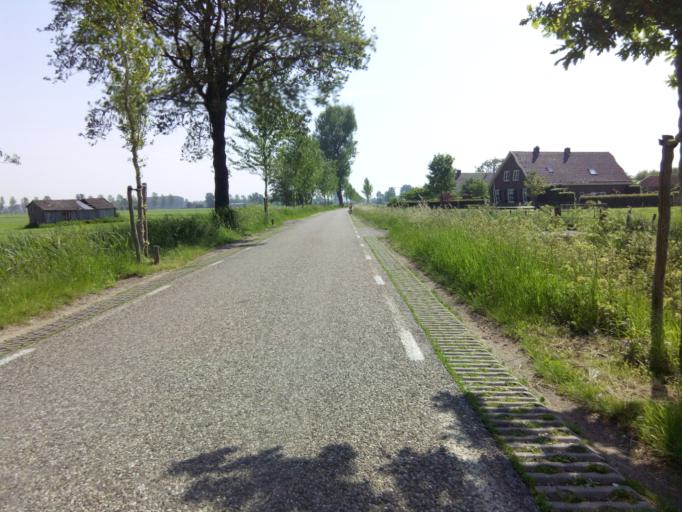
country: NL
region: Utrecht
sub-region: Gemeente Wijk bij Duurstede
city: Wijk bij Duurstede
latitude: 51.9868
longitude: 5.3844
